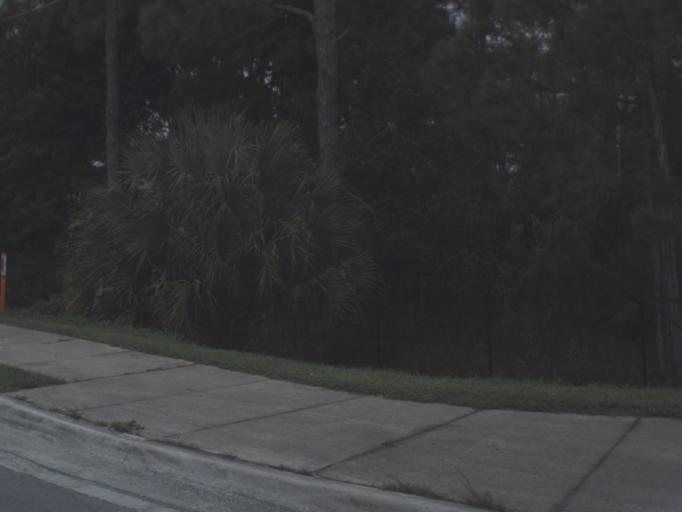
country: US
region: Florida
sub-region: Collier County
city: Lely Resort
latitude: 26.1222
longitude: -81.6871
